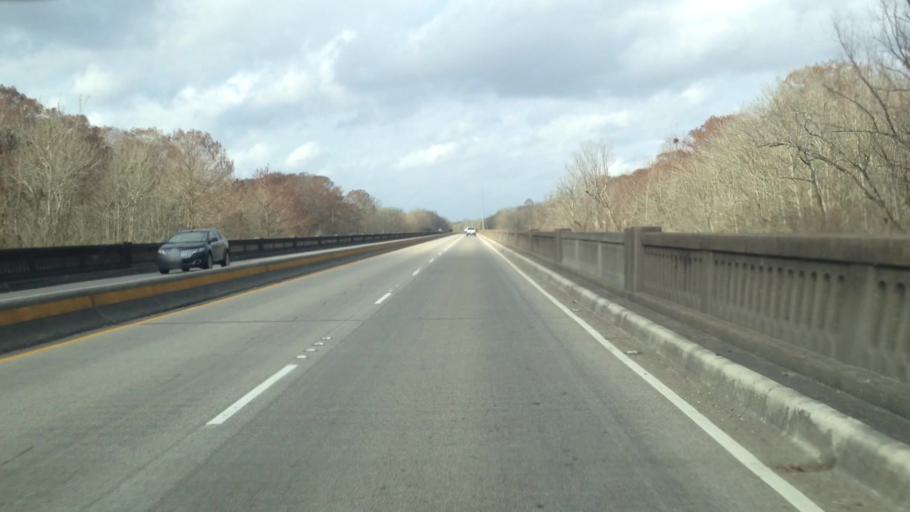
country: US
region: Louisiana
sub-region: Saint Landry Parish
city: Krotz Springs
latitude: 30.5524
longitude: -91.7198
